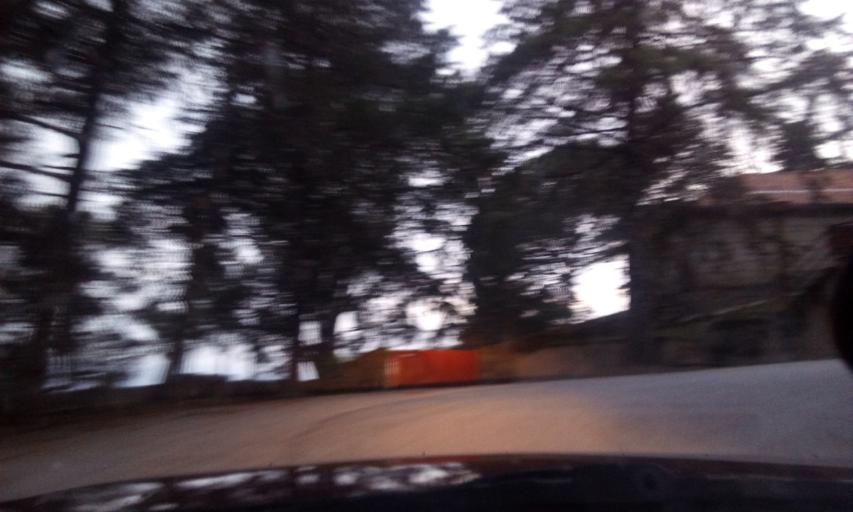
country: PT
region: Guarda
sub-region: Fornos de Algodres
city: Fornos de Algodres
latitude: 40.6210
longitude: -7.5438
